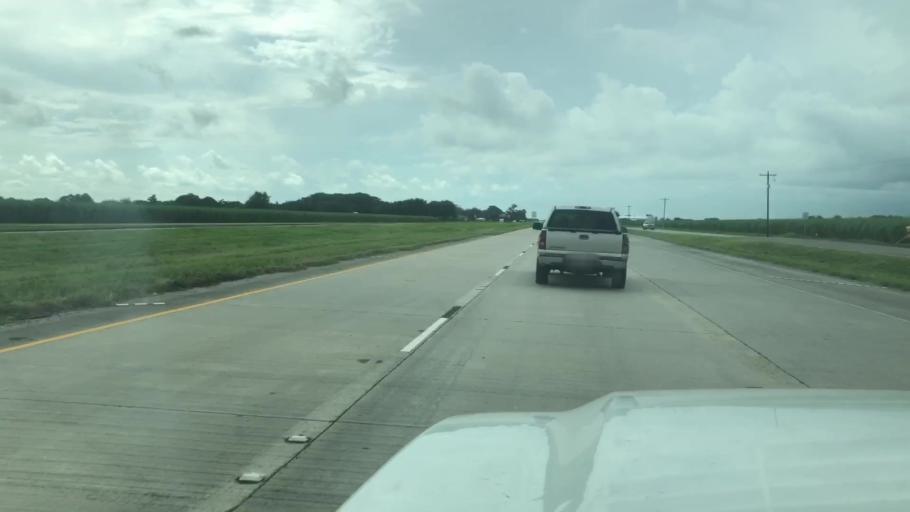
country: US
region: Louisiana
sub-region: Iberia Parish
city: Jeanerette
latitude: 29.9232
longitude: -91.7336
